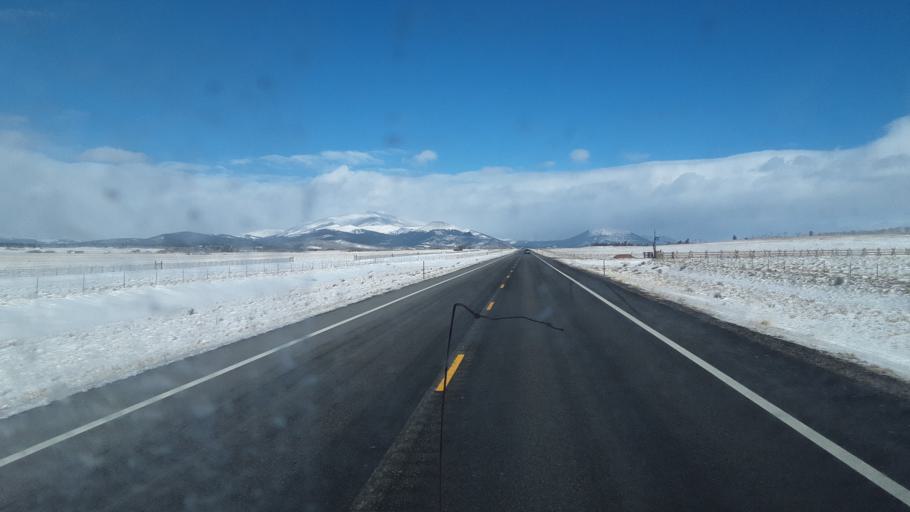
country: US
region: Colorado
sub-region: Park County
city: Fairplay
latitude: 39.1866
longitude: -105.9979
